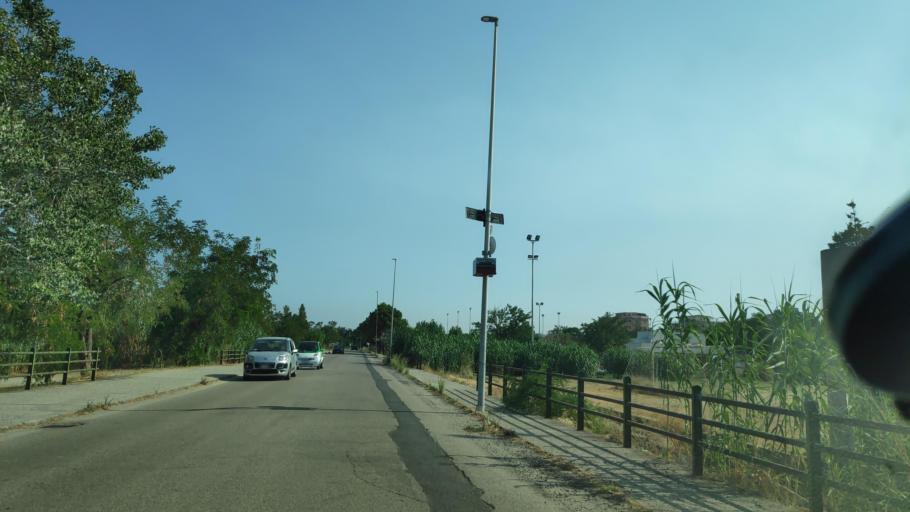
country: IT
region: Calabria
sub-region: Provincia di Catanzaro
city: Badolato Marina
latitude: 38.5752
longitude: 16.5684
